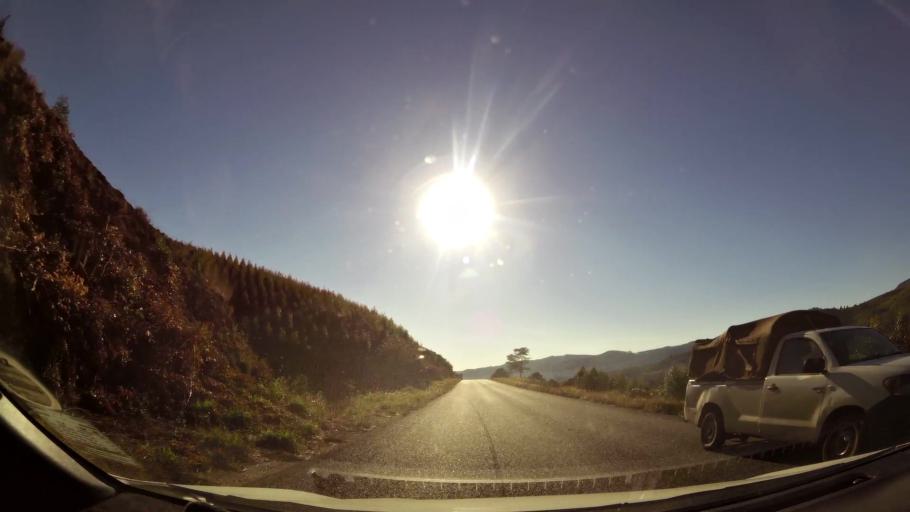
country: ZA
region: Limpopo
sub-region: Mopani District Municipality
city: Tzaneen
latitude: -23.9436
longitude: 30.0180
